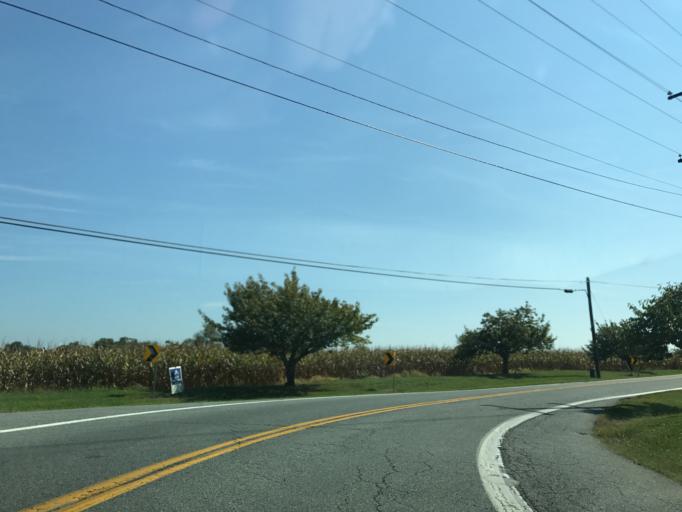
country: US
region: Maryland
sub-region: Cecil County
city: Elkton
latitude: 39.5358
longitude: -75.8072
